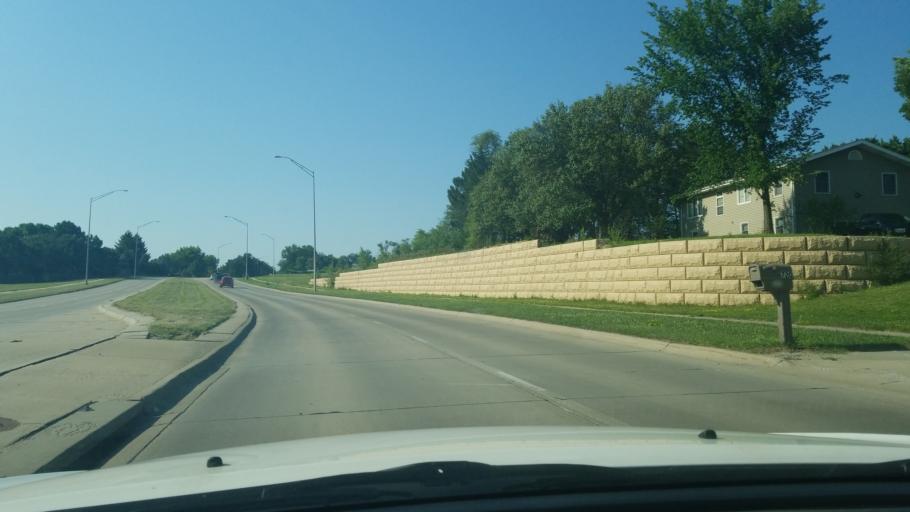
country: US
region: Nebraska
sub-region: Lancaster County
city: Lincoln
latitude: 40.7425
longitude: -96.6055
